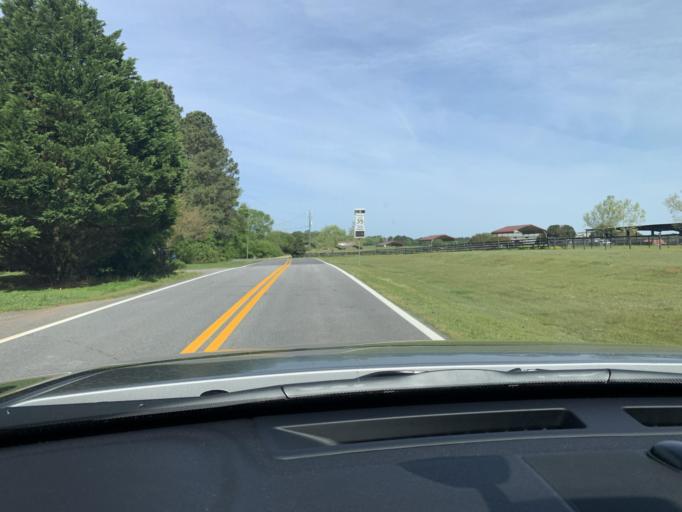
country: US
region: Georgia
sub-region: Oconee County
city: Watkinsville
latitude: 33.8167
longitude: -83.4281
